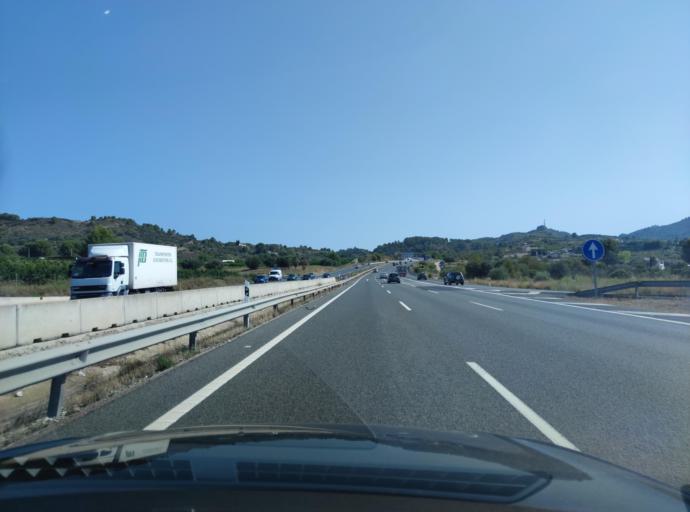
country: ES
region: Valencia
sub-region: Provincia de Valencia
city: Rotgla y Corbera
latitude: 39.0179
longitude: -0.5566
